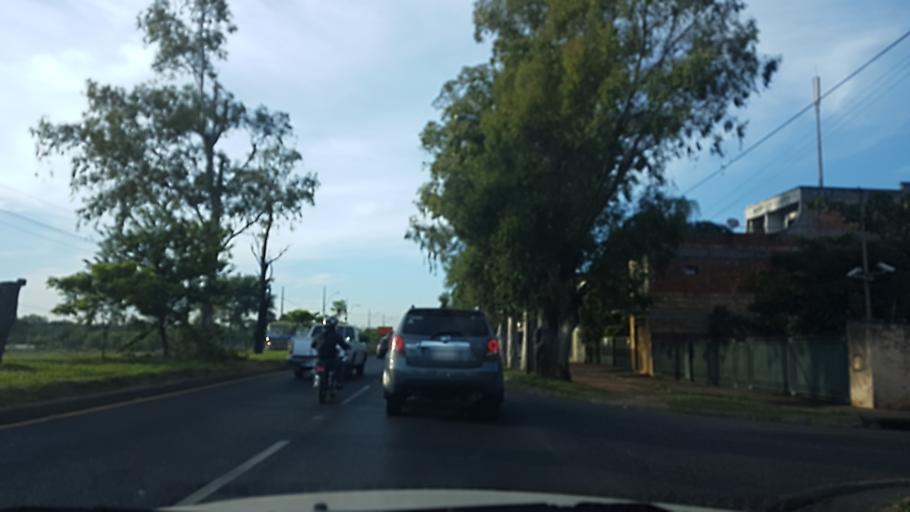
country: PY
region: Central
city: Fernando de la Mora
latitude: -25.2684
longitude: -57.5466
